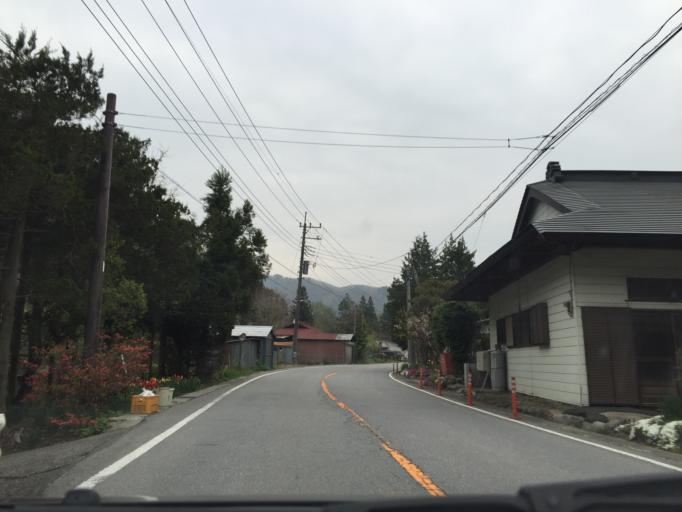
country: JP
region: Tochigi
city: Nikko
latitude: 36.9758
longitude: 139.6905
